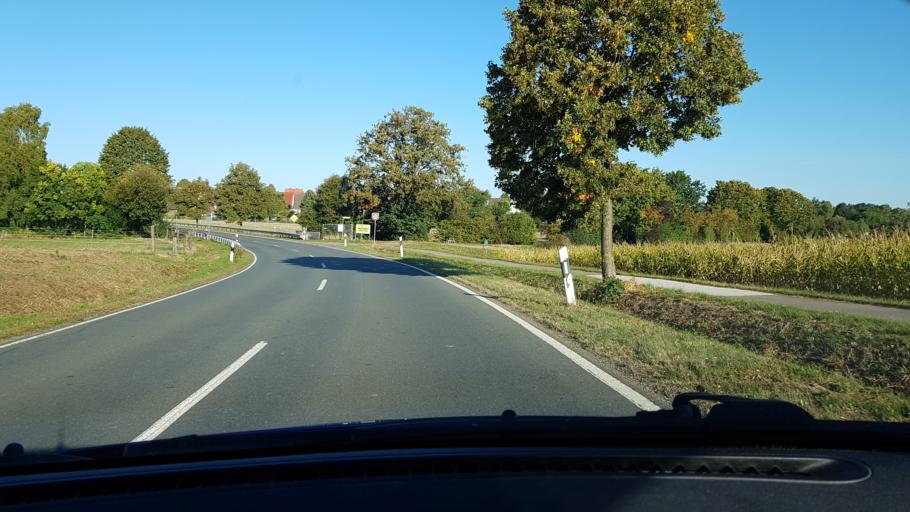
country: DE
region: Lower Saxony
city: Hulsede
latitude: 52.2515
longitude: 9.3710
